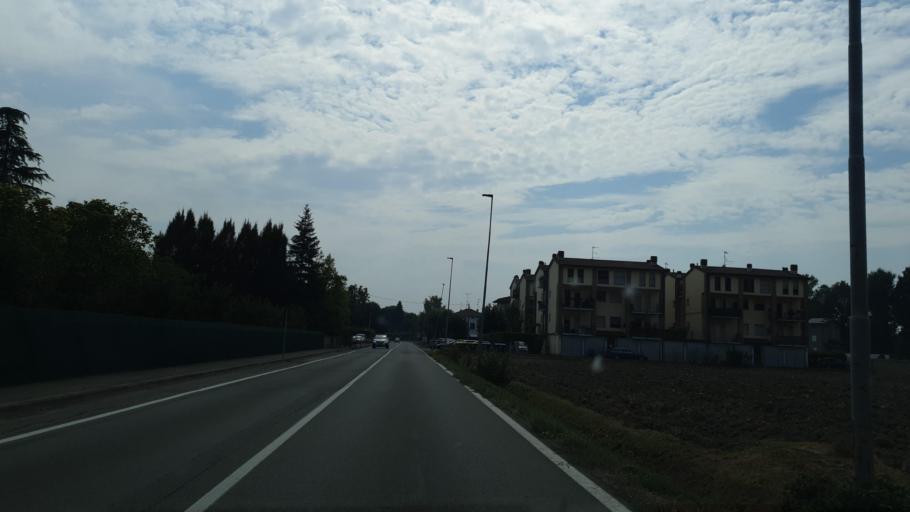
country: IT
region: Emilia-Romagna
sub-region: Provincia di Parma
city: San Secondo Parmense
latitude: 44.8745
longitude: 10.2508
